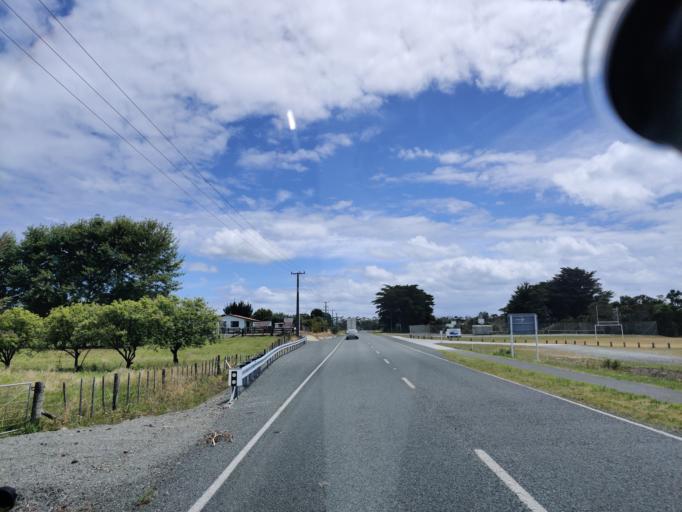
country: NZ
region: Northland
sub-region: Far North District
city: Kaitaia
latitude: -34.8310
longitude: 173.1292
